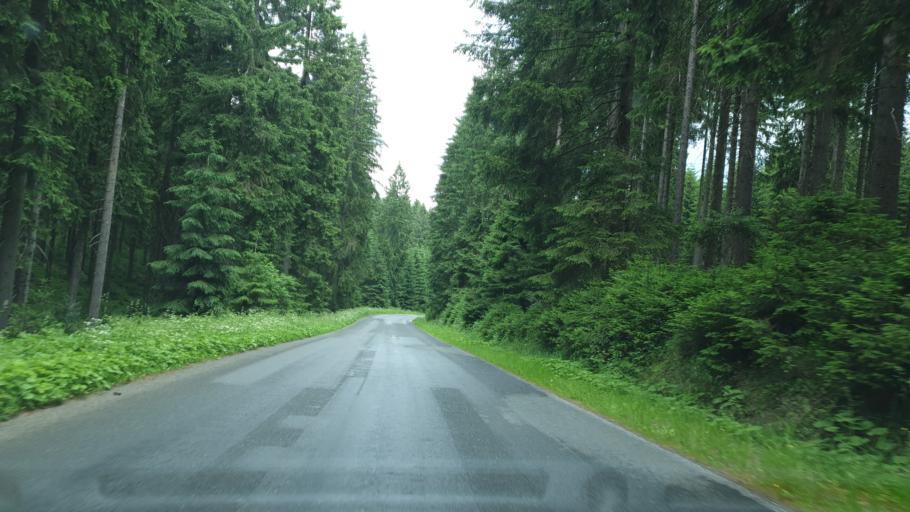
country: DE
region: Saxony
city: Tannenbergsthal
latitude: 50.4193
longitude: 12.4484
